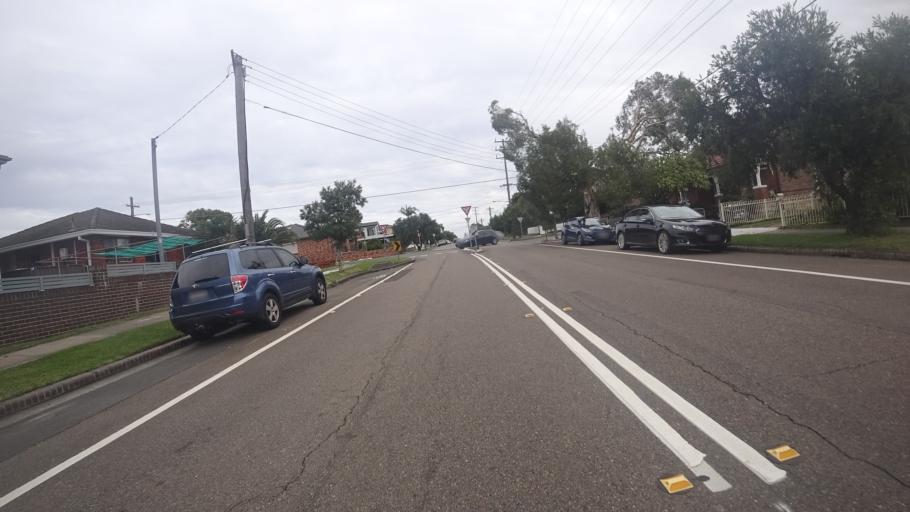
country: AU
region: New South Wales
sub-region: Rockdale
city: Bardwell Valley
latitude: -33.9386
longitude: 151.1335
